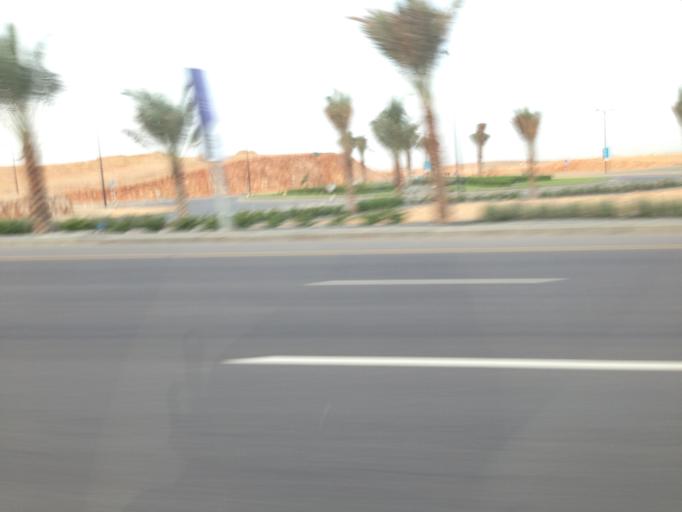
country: OM
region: Muhafazat Masqat
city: Bawshar
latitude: 23.5782
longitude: 58.3327
